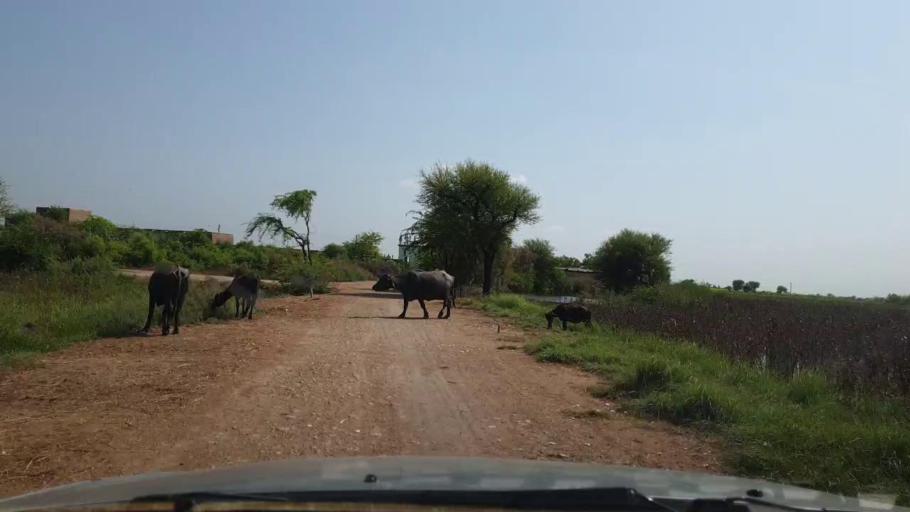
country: PK
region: Sindh
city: Rajo Khanani
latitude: 25.0180
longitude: 68.7994
